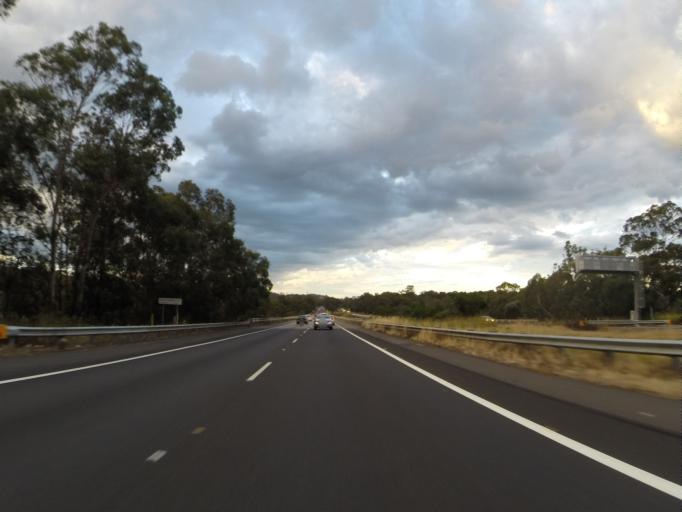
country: AU
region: New South Wales
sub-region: Wollondilly
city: Douglas Park
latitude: -34.1932
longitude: 150.7111
